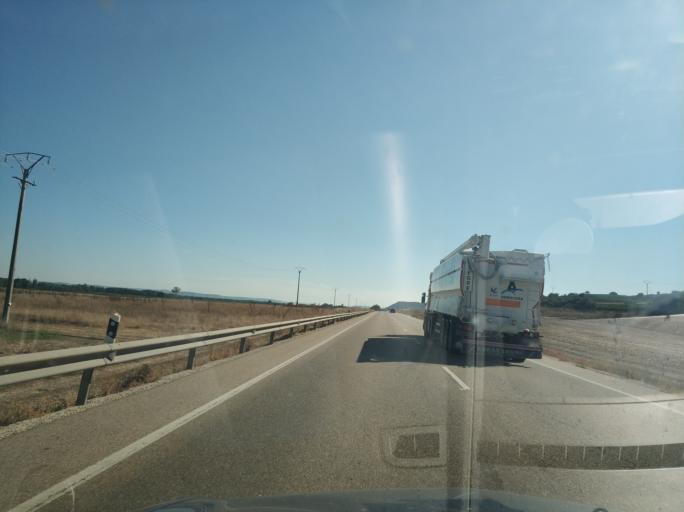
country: ES
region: Castille and Leon
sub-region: Provincia de Valladolid
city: Quintanilla de Arriba
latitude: 41.6223
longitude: -4.2459
